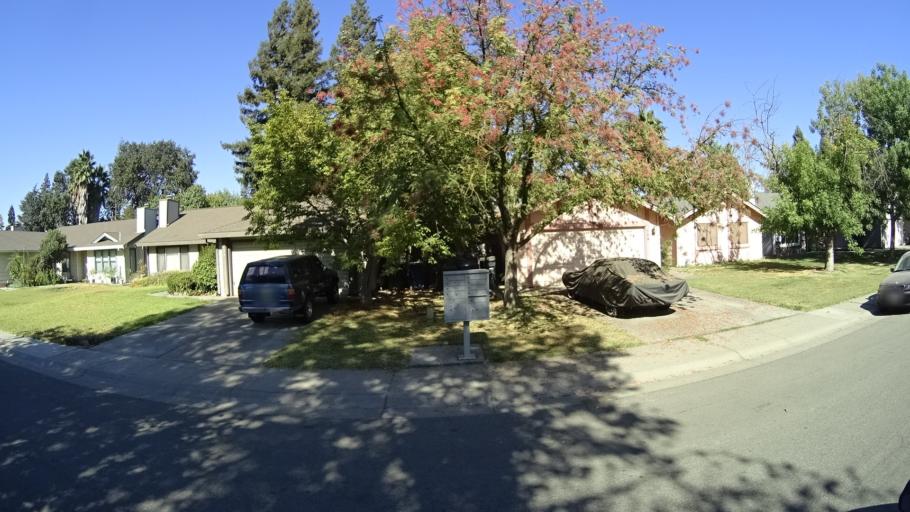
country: US
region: California
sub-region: Sacramento County
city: Parkway
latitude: 38.4876
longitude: -121.5351
